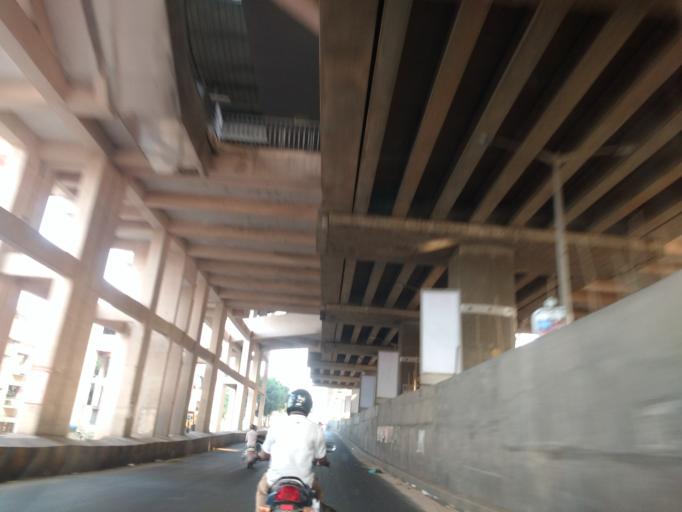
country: IN
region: Karnataka
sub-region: Bangalore Urban
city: Bangalore
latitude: 13.0230
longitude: 77.5501
